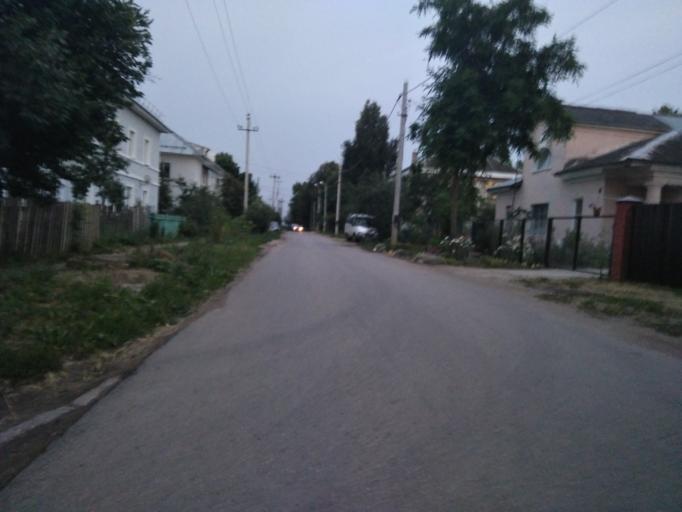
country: RU
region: Tula
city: Lomintsevskiy
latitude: 53.9324
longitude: 37.6230
